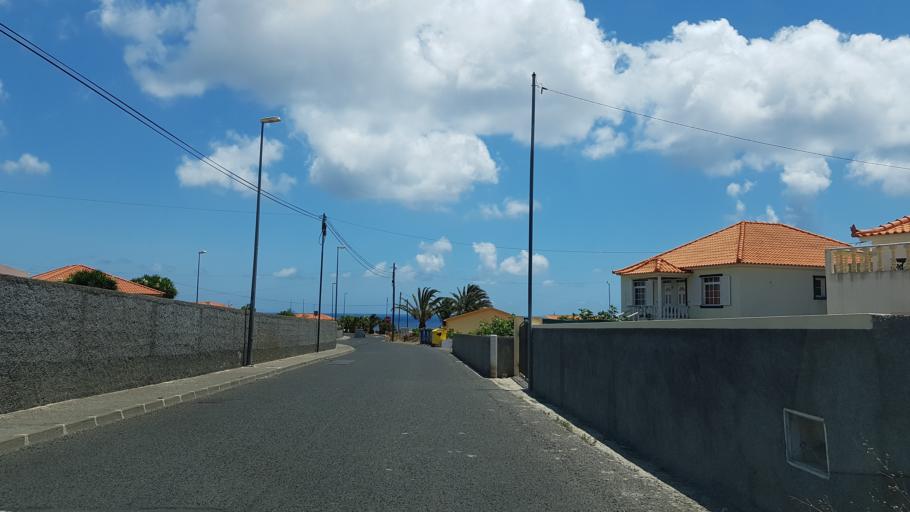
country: PT
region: Madeira
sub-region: Porto Santo
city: Vila de Porto Santo
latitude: 33.0543
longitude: -16.3637
